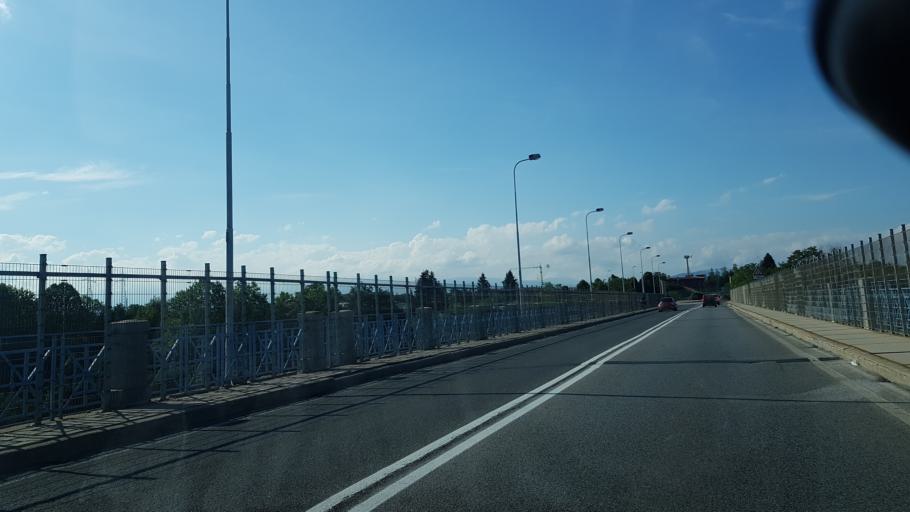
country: IT
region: Piedmont
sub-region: Provincia di Cuneo
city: Cuneo
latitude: 44.3965
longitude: 7.5396
